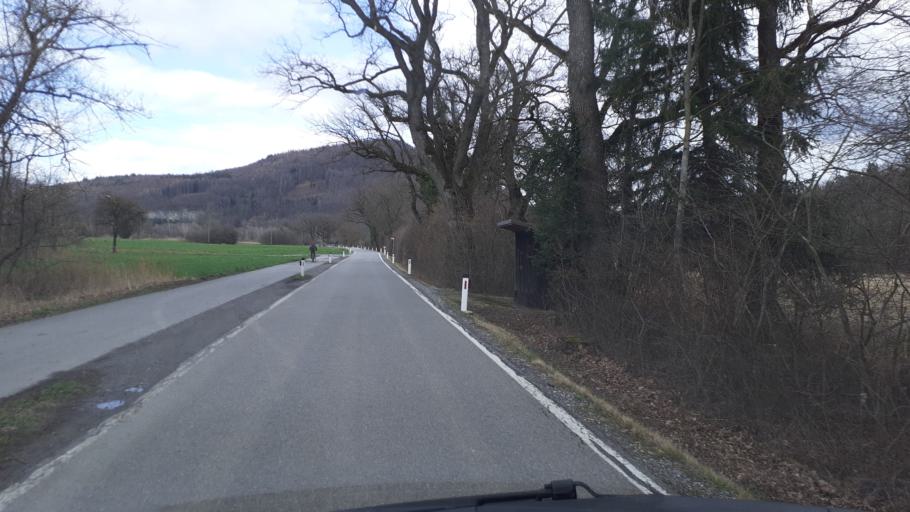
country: AT
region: Vorarlberg
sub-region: Politischer Bezirk Feldkirch
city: Koblach
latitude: 47.3191
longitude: 9.6162
